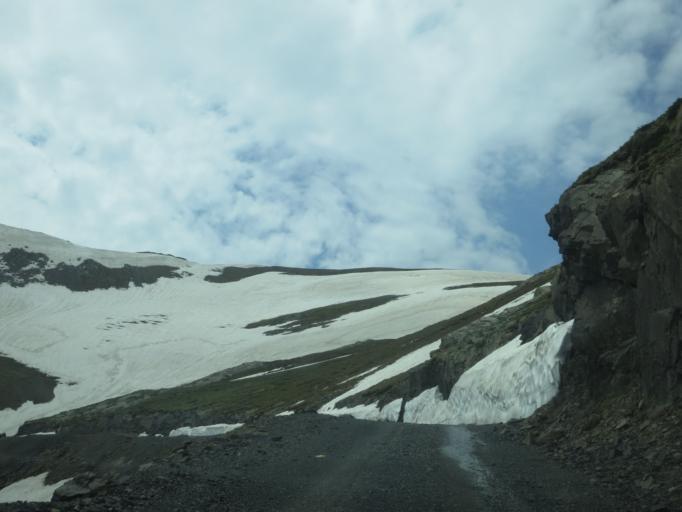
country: GE
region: Kakheti
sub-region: Telavi
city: Telavi
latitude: 42.2825
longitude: 45.5019
